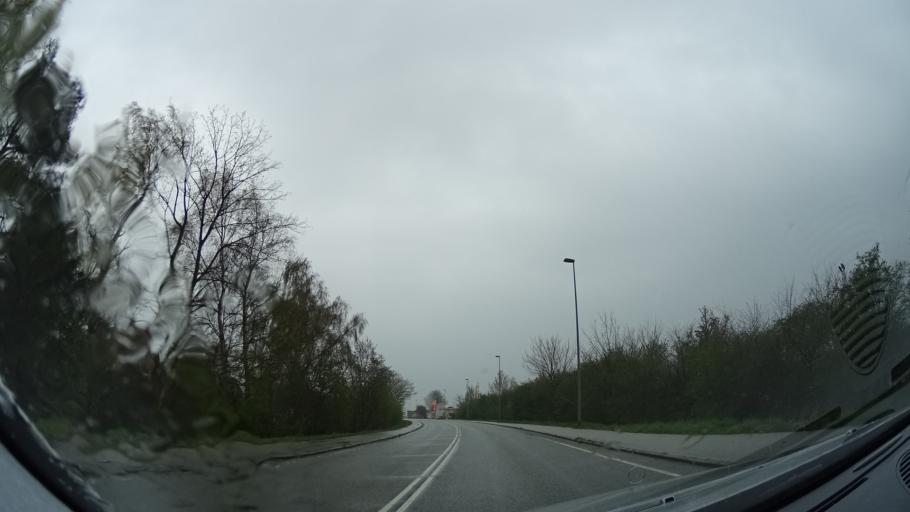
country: DK
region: Zealand
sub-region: Odsherred Kommune
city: Hojby
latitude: 55.8510
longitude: 11.5755
